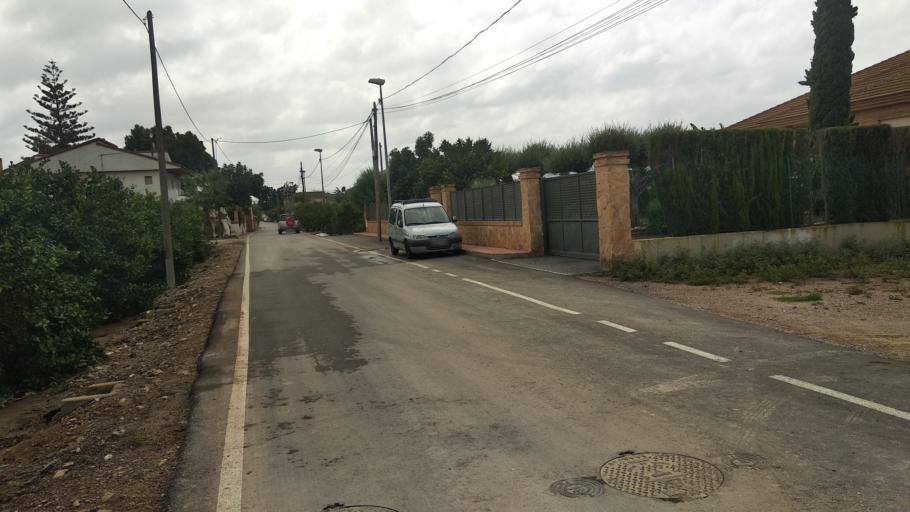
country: ES
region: Murcia
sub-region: Murcia
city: Santomera
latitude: 38.0407
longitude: -1.0340
